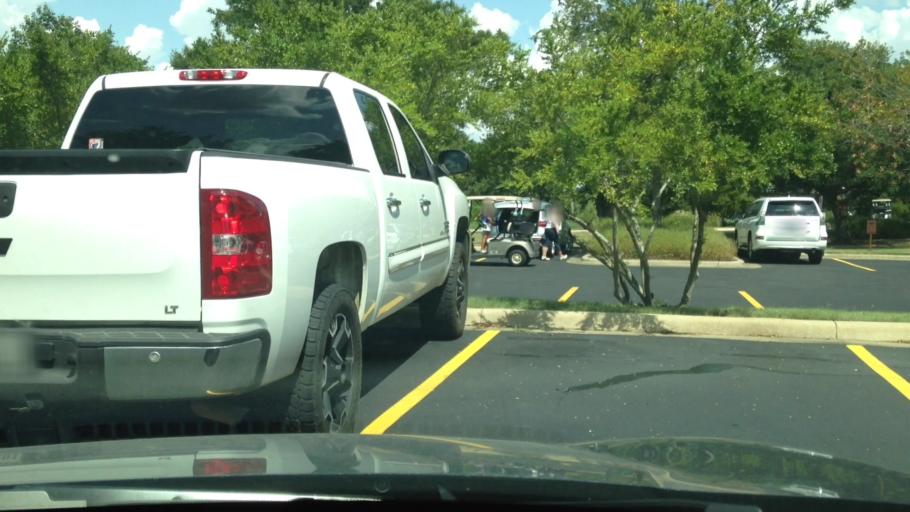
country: US
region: Texas
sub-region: Williamson County
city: Leander
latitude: 30.6393
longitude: -97.7942
